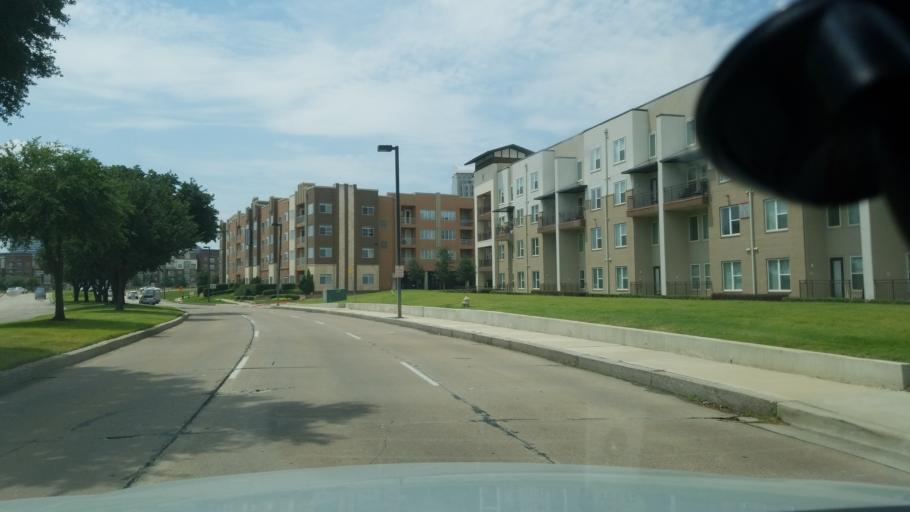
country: US
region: Texas
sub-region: Dallas County
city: Irving
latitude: 32.8730
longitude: -96.9336
